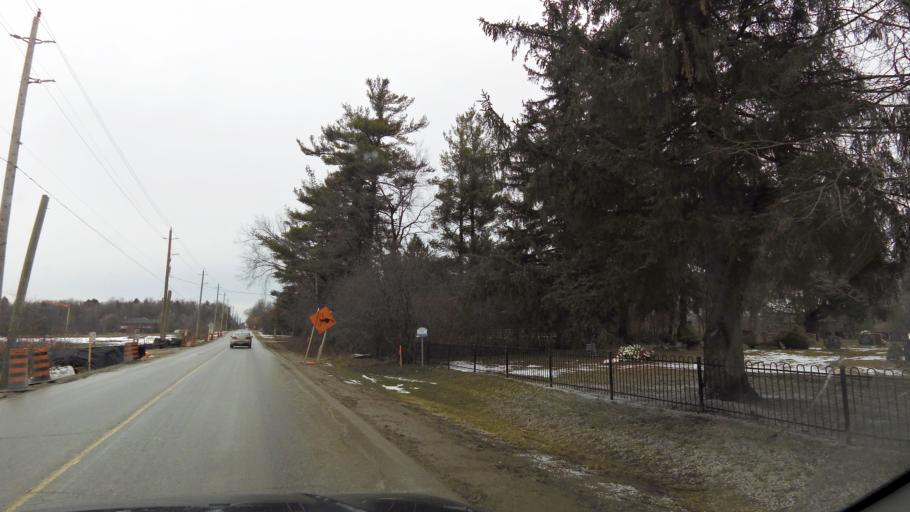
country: CA
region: Ontario
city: Vaughan
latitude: 43.8352
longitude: -79.6626
